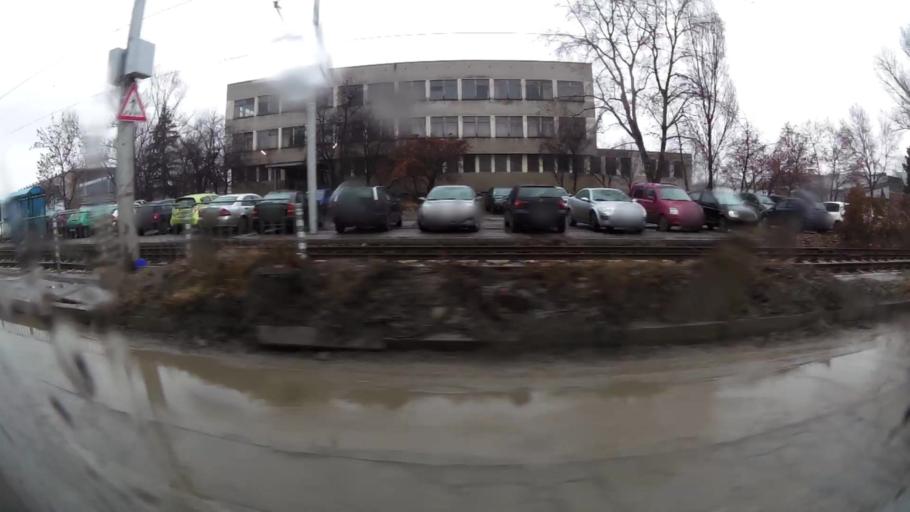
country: BG
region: Sofia-Capital
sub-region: Stolichna Obshtina
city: Sofia
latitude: 42.6598
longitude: 23.4151
